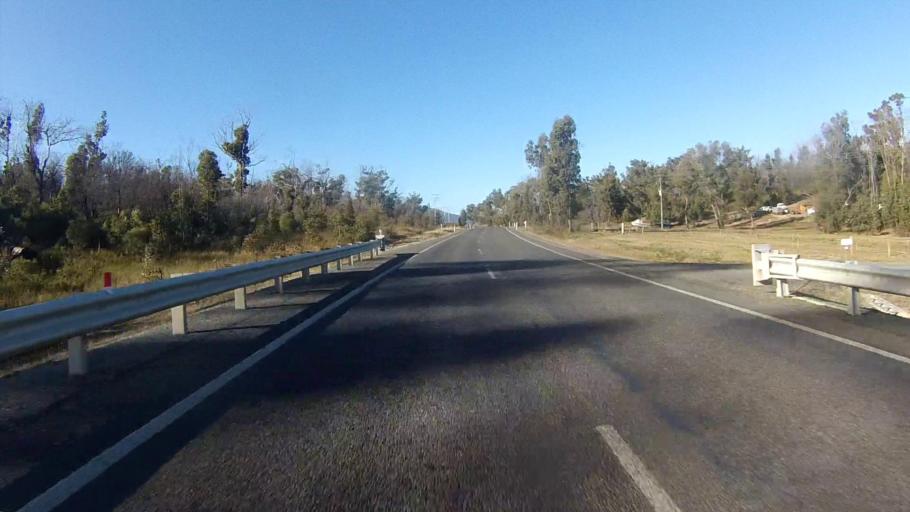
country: AU
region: Tasmania
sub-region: Sorell
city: Sorell
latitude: -42.9286
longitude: 147.8434
